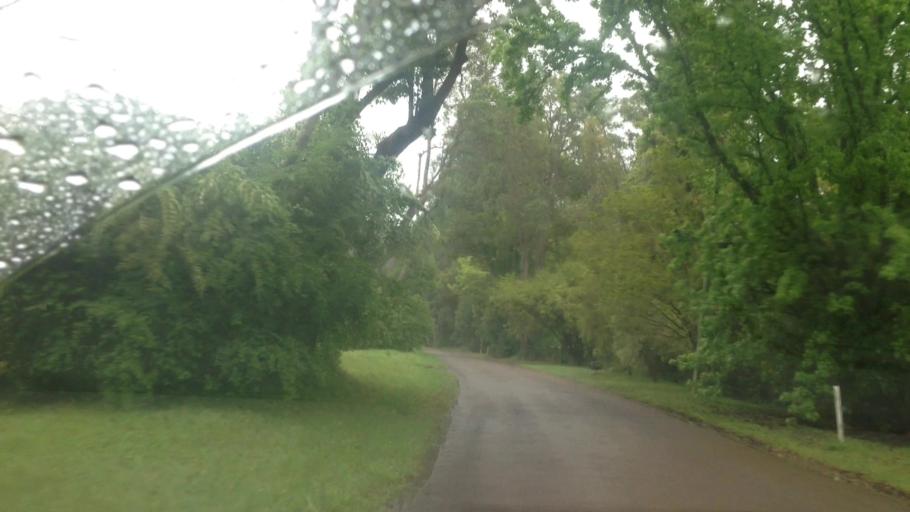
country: AU
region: New South Wales
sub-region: Wyong Shire
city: Little Jilliby
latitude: -33.1884
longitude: 151.3617
